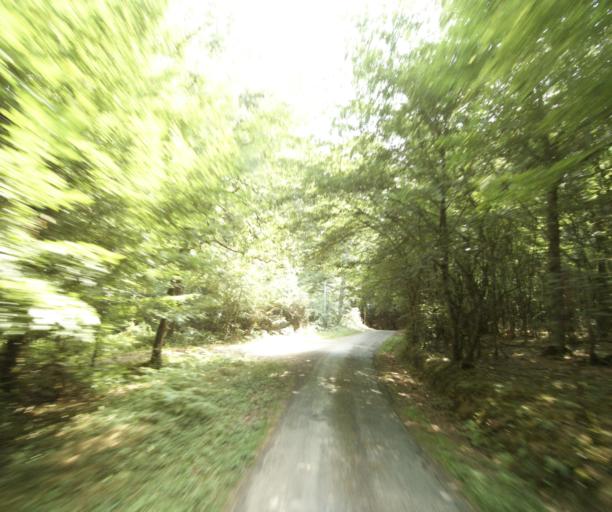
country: FR
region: Bourgogne
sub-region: Departement de Saone-et-Loire
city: Gueugnon
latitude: 46.6038
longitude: 4.0225
